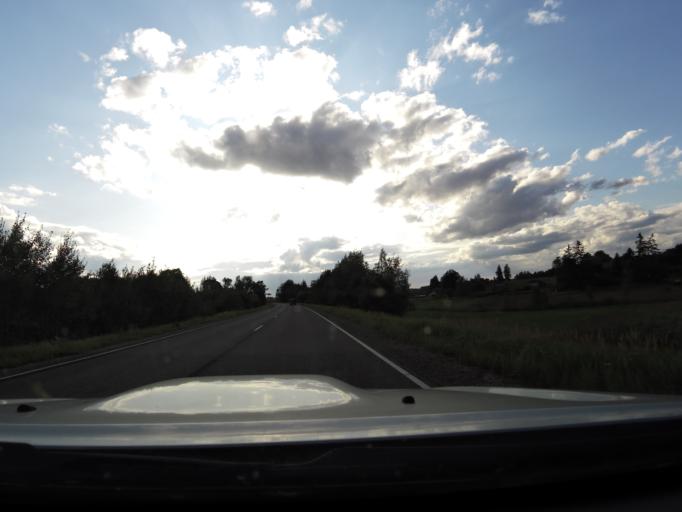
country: LV
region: Nereta
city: Nereta
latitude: 56.1949
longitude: 25.4488
